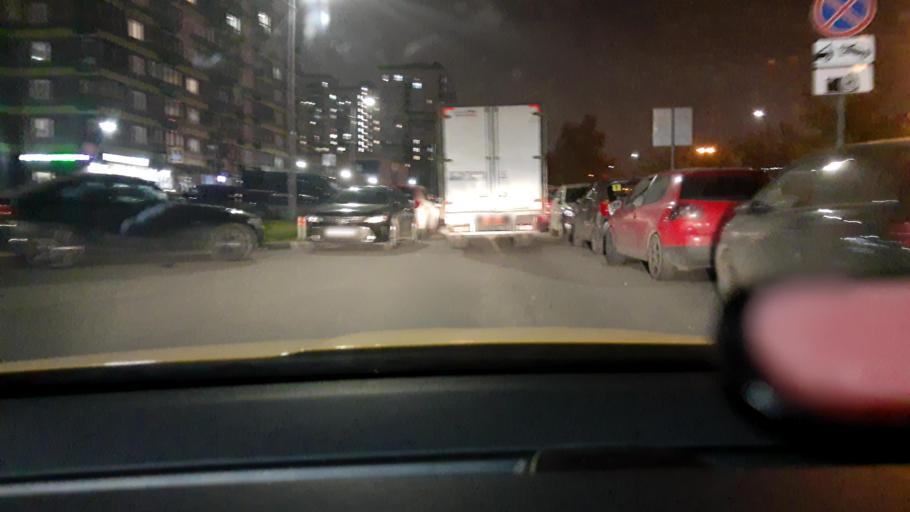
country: RU
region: Moscow
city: Khimki
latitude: 55.8668
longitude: 37.3983
